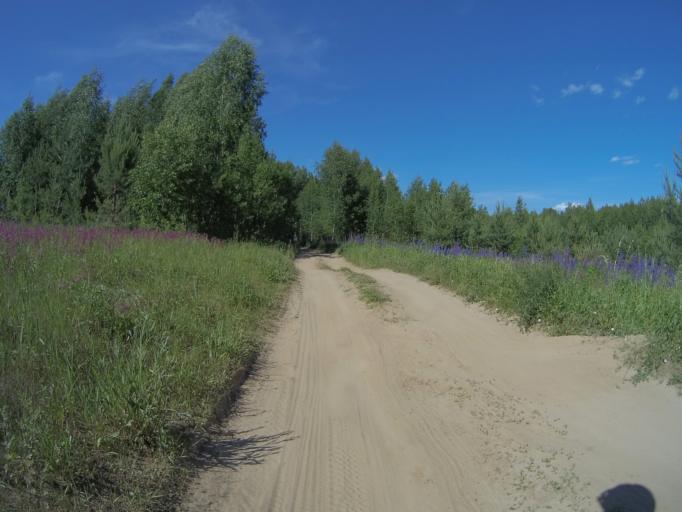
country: RU
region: Vladimir
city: Raduzhnyy
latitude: 55.9914
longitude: 40.3726
